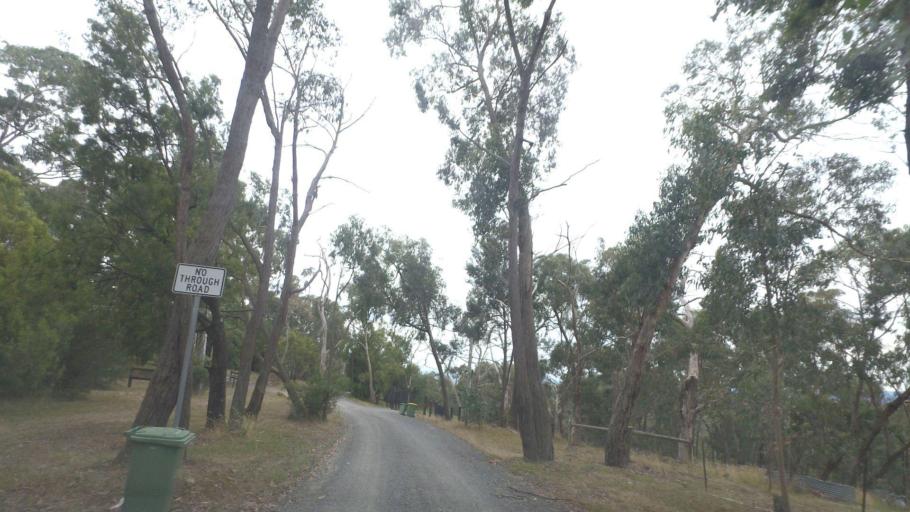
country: AU
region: Victoria
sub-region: Yarra Ranges
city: Mount Evelyn
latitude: -37.7578
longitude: 145.3991
